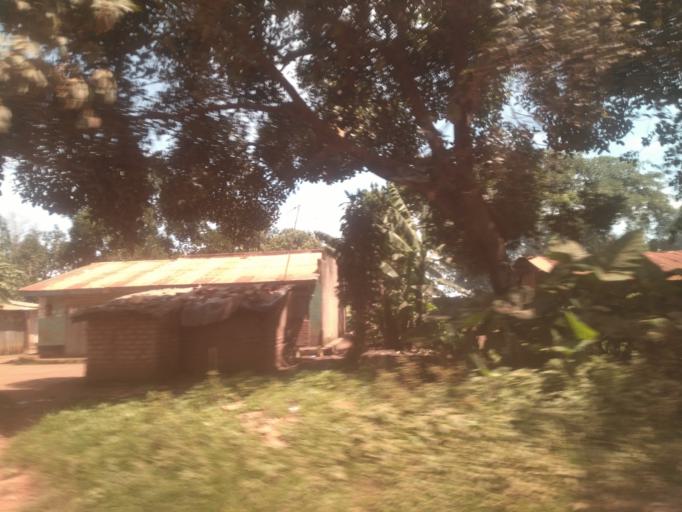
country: UG
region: Central Region
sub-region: Wakiso District
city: Entebbe
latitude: 0.0343
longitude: 32.4372
